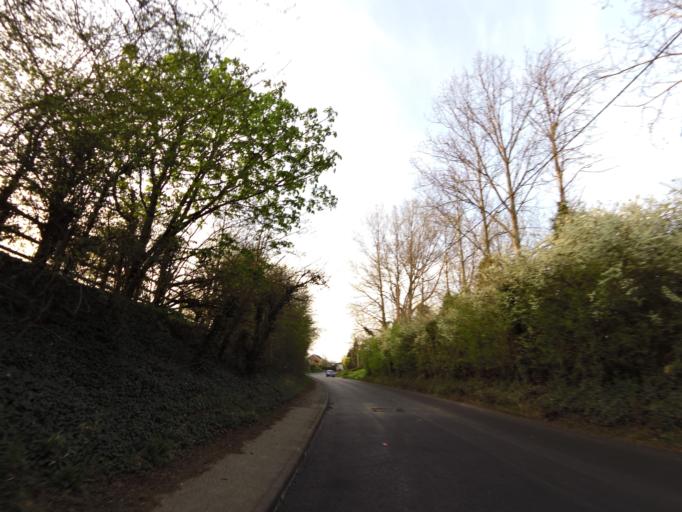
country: GB
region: England
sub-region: Suffolk
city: Ipswich
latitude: 52.1165
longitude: 1.1873
